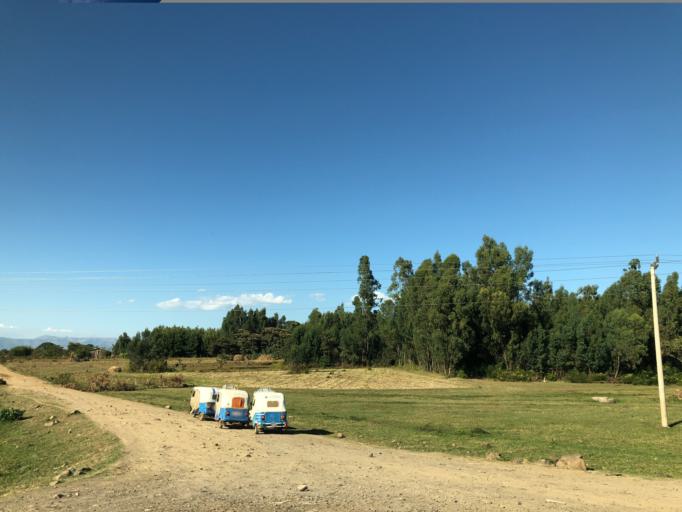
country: ET
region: Amhara
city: Werota
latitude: 11.9312
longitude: 37.8365
